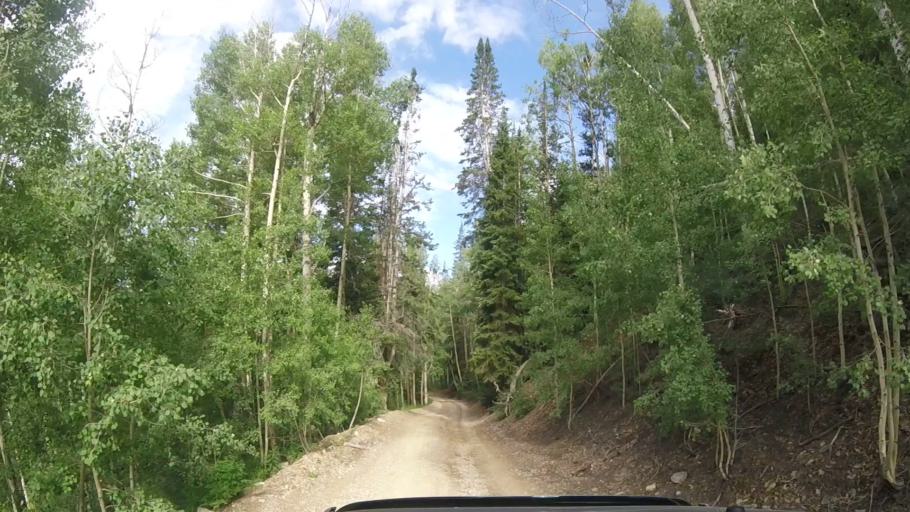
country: US
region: Colorado
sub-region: San Miguel County
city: Telluride
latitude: 37.8594
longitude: -107.7942
